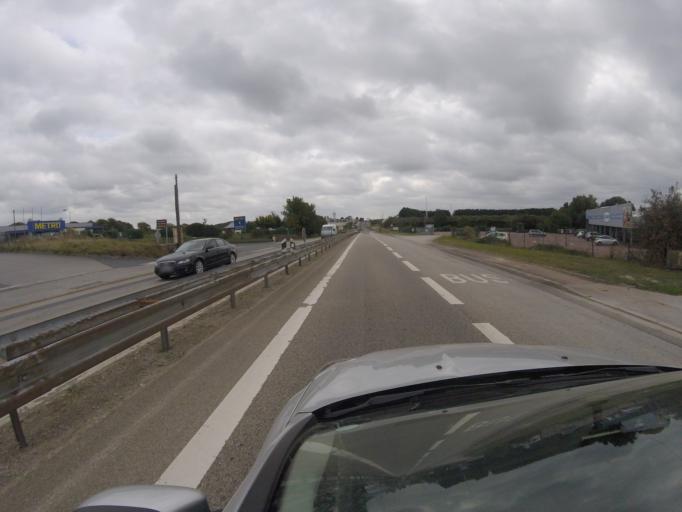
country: FR
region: Lower Normandy
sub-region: Departement de la Manche
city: La Glacerie
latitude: 49.6076
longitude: -1.5997
